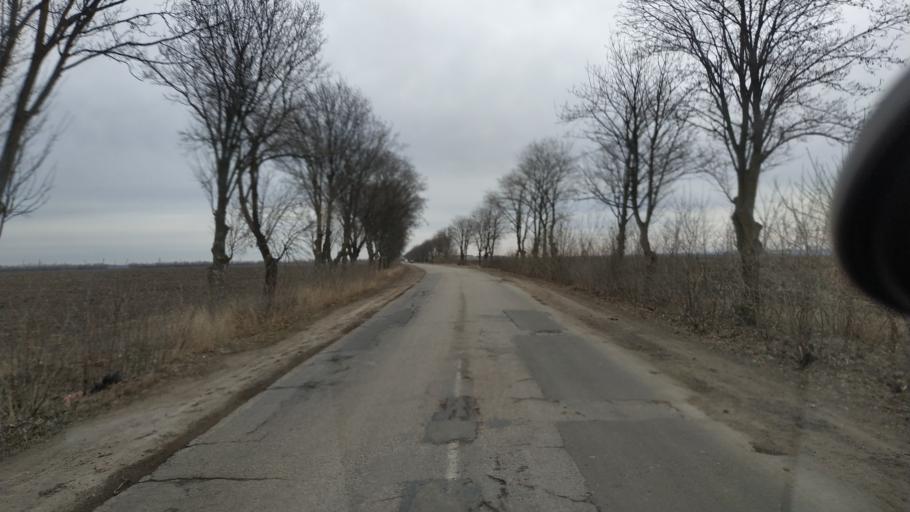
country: MD
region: Telenesti
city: Cocieri
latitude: 47.2660
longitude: 29.0877
